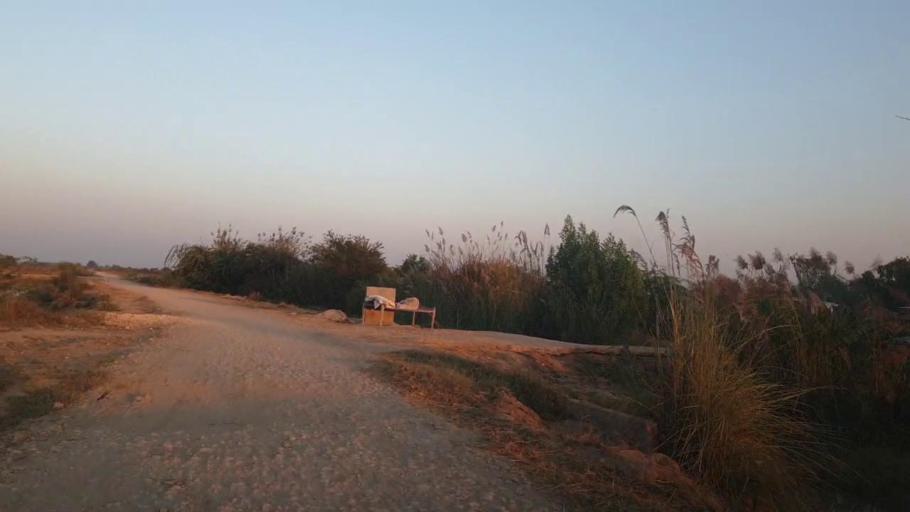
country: PK
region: Sindh
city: Mirpur Sakro
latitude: 24.4199
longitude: 67.5798
